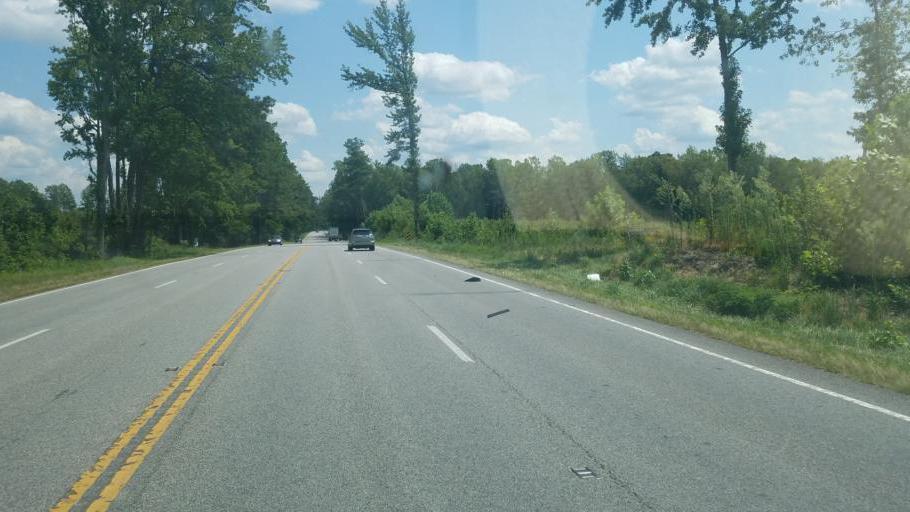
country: US
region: Virginia
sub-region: Sussex County
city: Waverly
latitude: 37.0927
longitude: -77.1756
